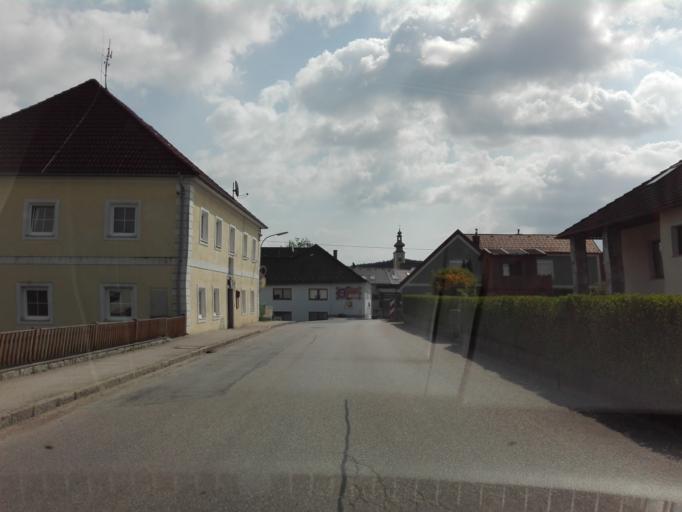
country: AT
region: Upper Austria
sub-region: Politischer Bezirk Perg
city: Perg
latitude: 48.2676
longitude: 14.7095
